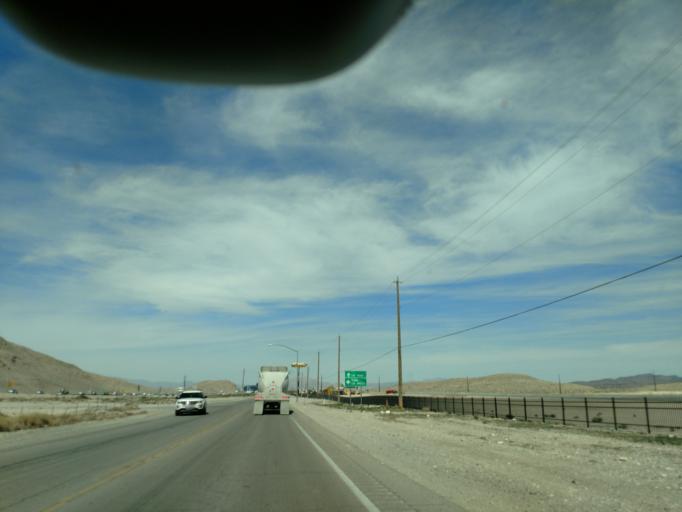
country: US
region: Nevada
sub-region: Clark County
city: Enterprise
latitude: 35.9293
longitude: -115.1924
